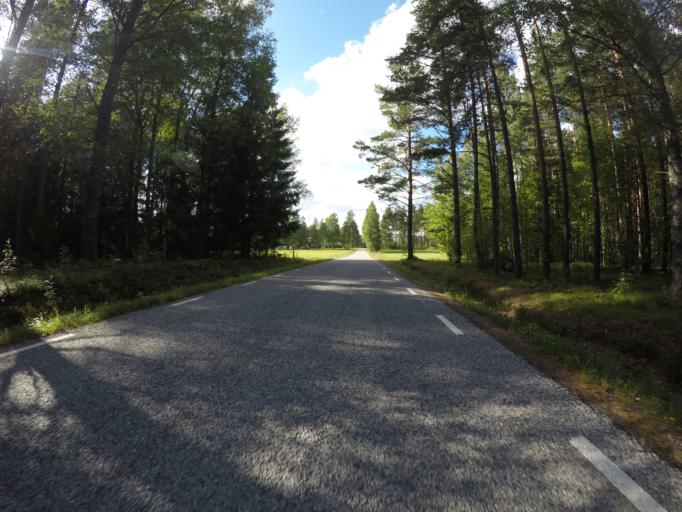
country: SE
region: OErebro
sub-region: Hallefors Kommun
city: Haellefors
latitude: 59.9090
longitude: 14.5497
